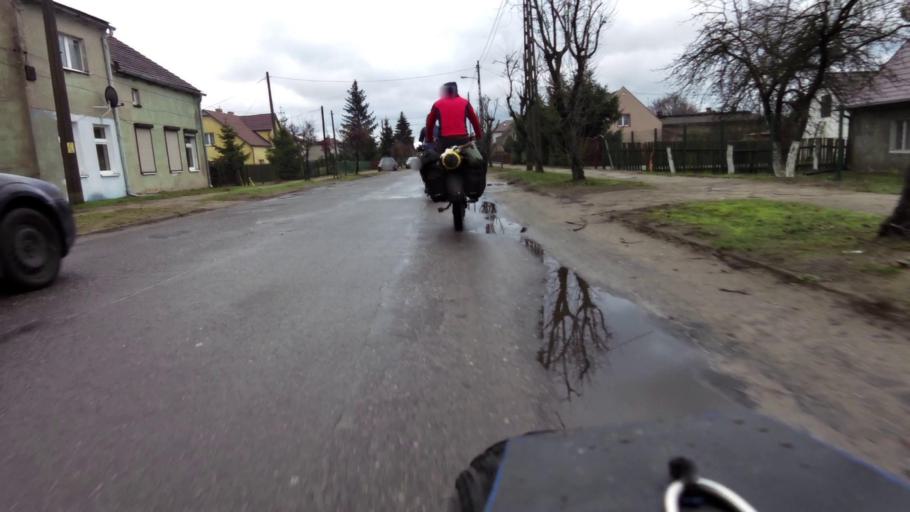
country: PL
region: Lubusz
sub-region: Powiat gorzowski
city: Witnica
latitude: 52.6803
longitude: 14.8911
